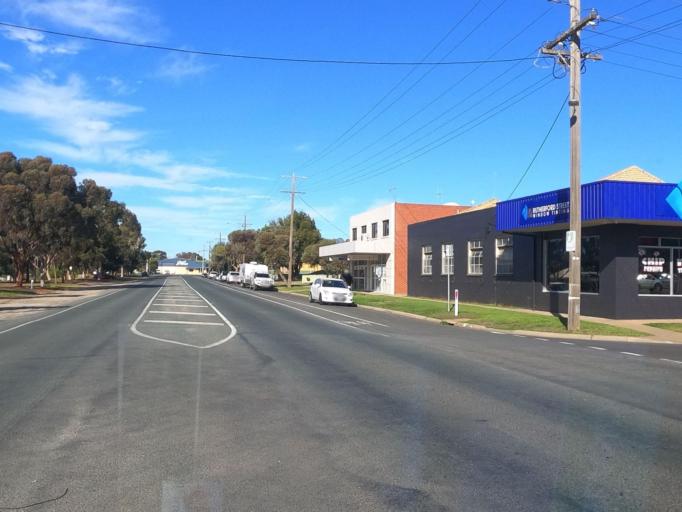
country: AU
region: Victoria
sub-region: Swan Hill
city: Swan Hill
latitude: -35.3425
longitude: 143.5620
